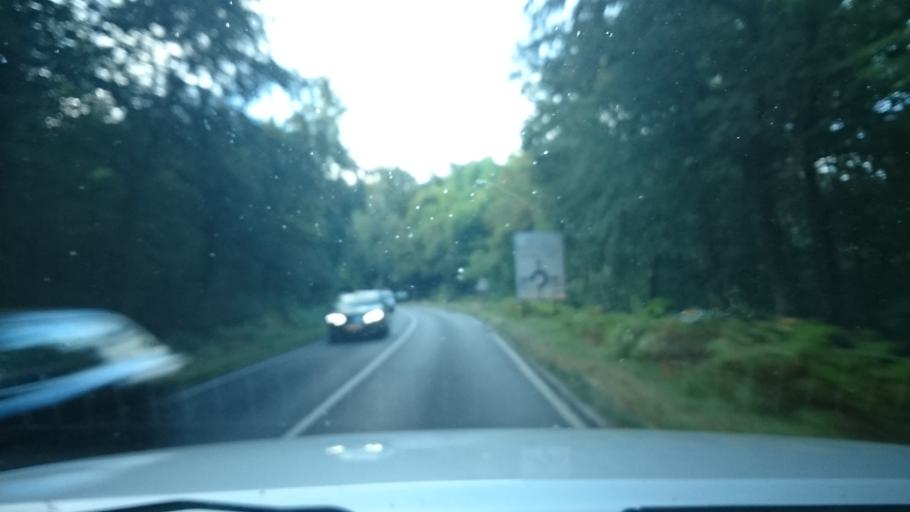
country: FR
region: Ile-de-France
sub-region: Departement de Seine-et-Marne
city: Samoreau
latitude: 48.4319
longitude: 2.7420
